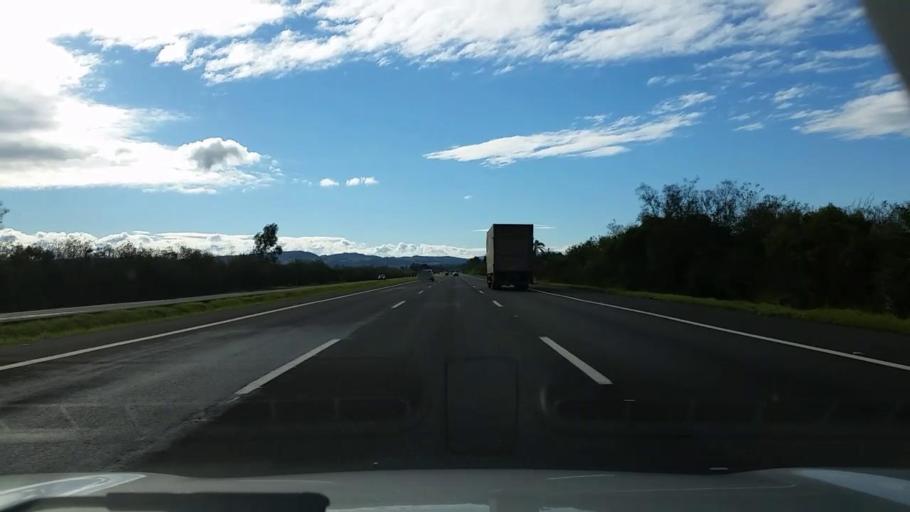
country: BR
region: Rio Grande do Sul
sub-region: Rolante
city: Rolante
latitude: -29.8825
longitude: -50.5319
